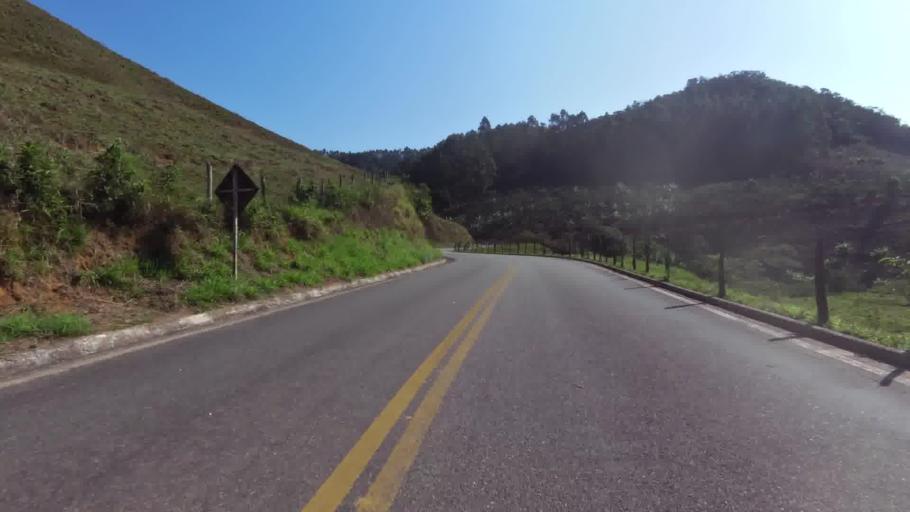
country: BR
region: Espirito Santo
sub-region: Alfredo Chaves
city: Alfredo Chaves
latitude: -20.5682
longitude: -40.8105
